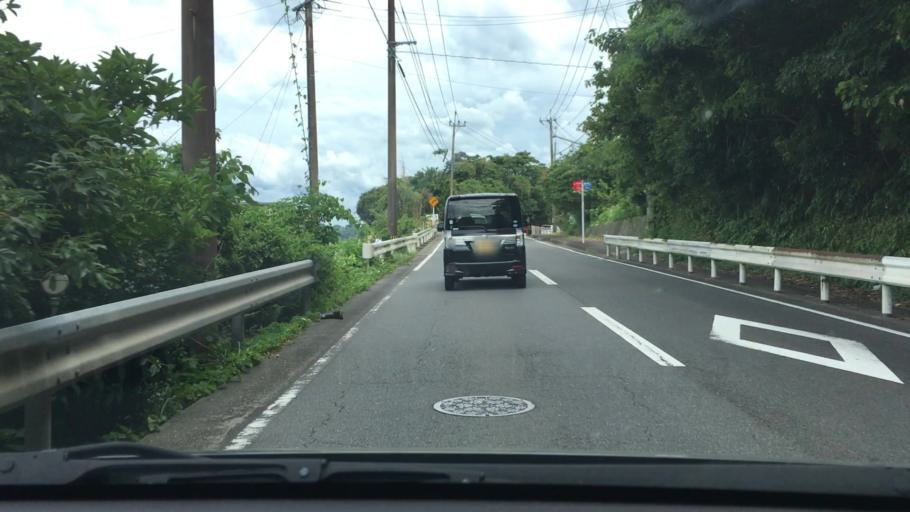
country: JP
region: Nagasaki
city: Togitsu
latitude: 32.9374
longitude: 129.7832
